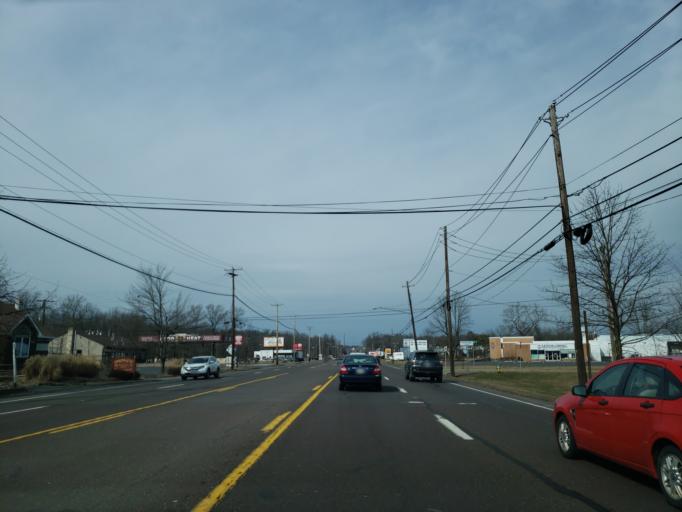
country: US
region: Pennsylvania
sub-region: Bucks County
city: Quakertown
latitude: 40.4514
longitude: -75.3630
